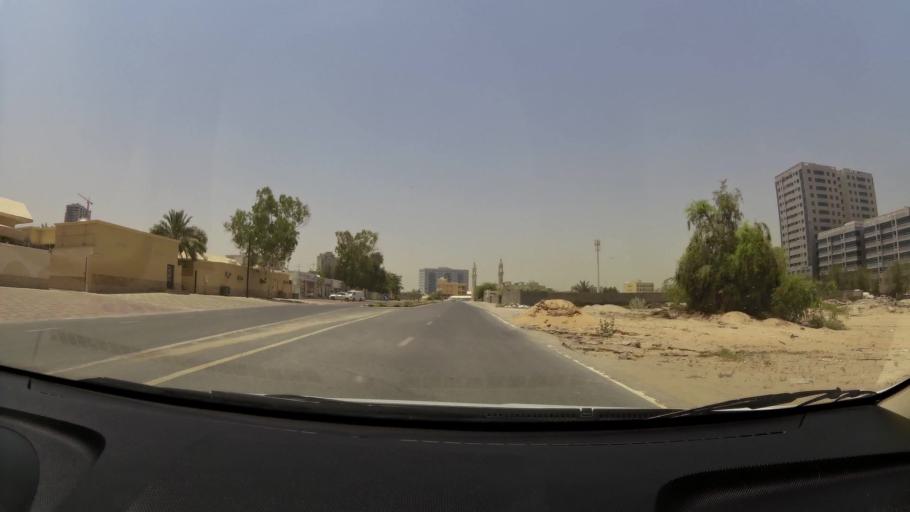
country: AE
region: Ajman
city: Ajman
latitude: 25.4032
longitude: 55.5087
